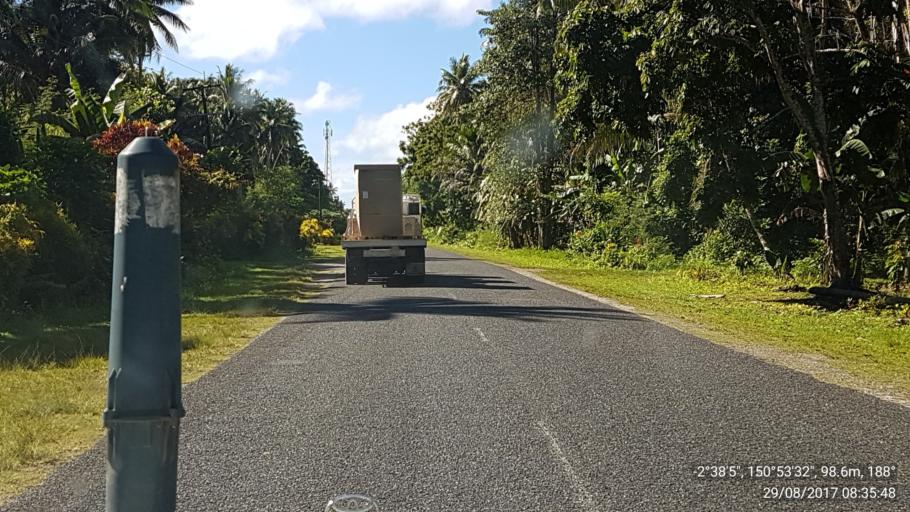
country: PG
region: New Ireland
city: Kavieng
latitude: -2.6350
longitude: 150.8925
